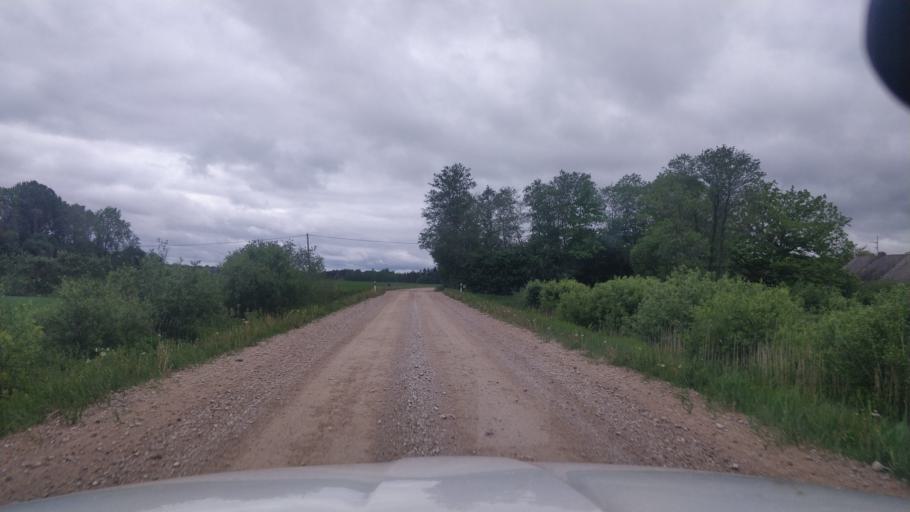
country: EE
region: Raplamaa
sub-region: Maerjamaa vald
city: Marjamaa
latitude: 58.7589
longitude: 24.2406
